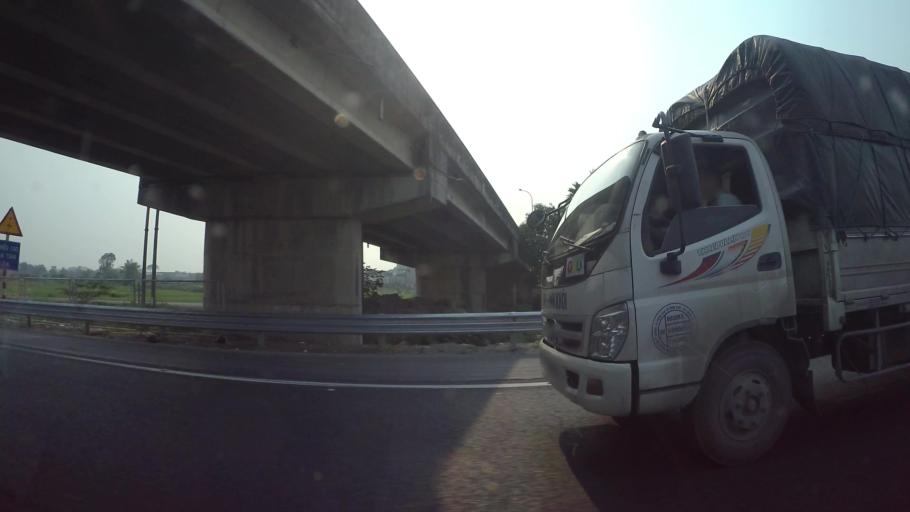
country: VN
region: Ha Noi
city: Van Dien
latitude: 20.9215
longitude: 105.8598
